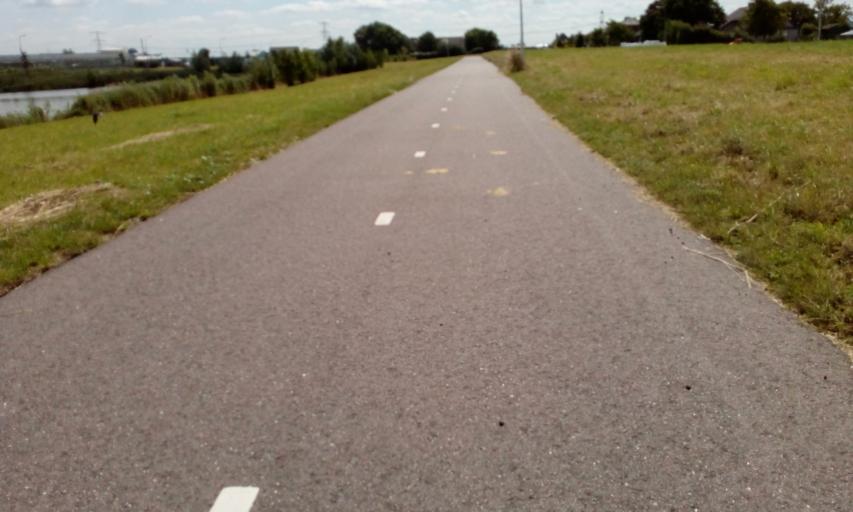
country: NL
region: South Holland
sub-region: Gemeente Westland
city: Kwintsheul
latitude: 52.0099
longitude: 4.2686
